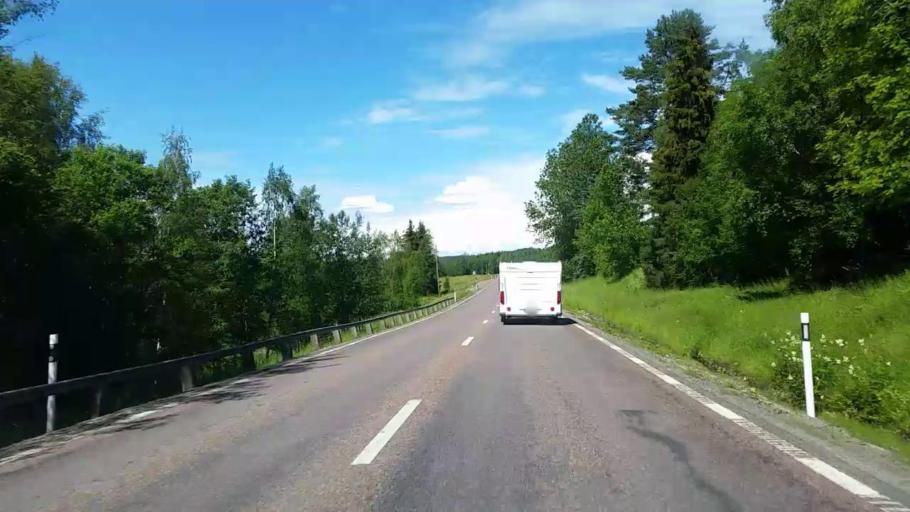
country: SE
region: Dalarna
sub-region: Rattviks Kommun
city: Raettvik
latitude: 60.9881
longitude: 15.2201
